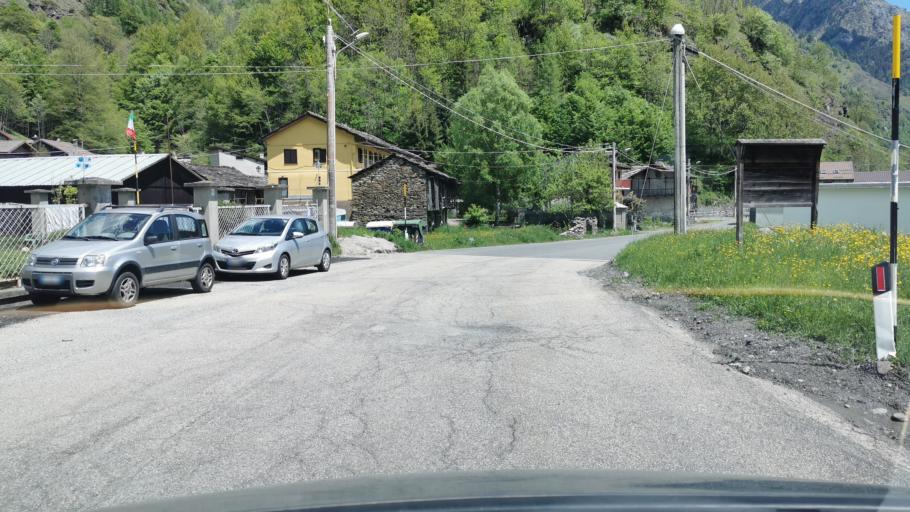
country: IT
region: Piedmont
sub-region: Provincia di Torino
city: Usseglio
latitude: 45.2309
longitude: 7.2036
